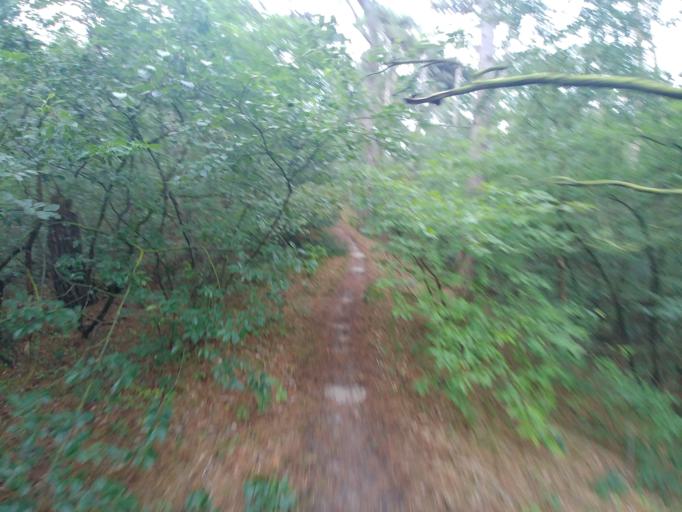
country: NL
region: North Holland
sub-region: Gemeente Alkmaar
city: Alkmaar
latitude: 52.6859
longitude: 4.6861
